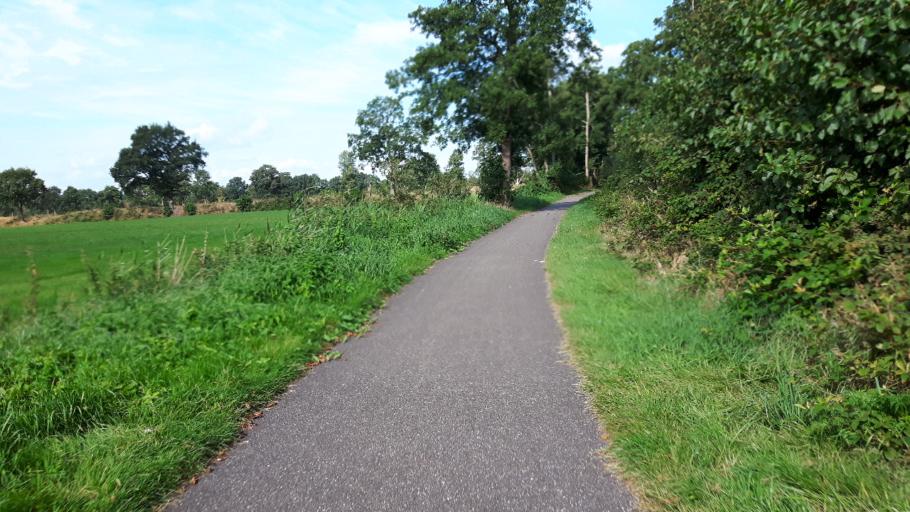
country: NL
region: Groningen
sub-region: Gemeente Leek
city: Leek
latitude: 53.1204
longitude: 6.4702
